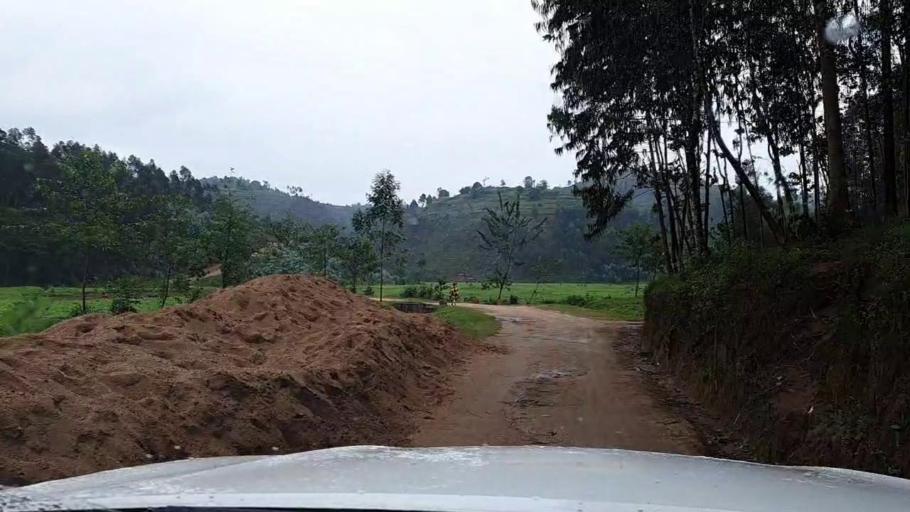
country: RW
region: Southern Province
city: Nzega
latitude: -2.4702
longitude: 29.5022
